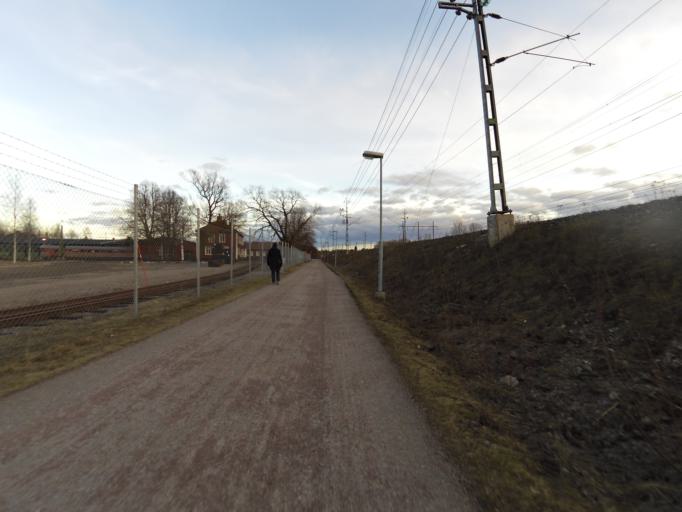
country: SE
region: Gaevleborg
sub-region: Gavle Kommun
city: Gavle
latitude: 60.6628
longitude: 17.1692
